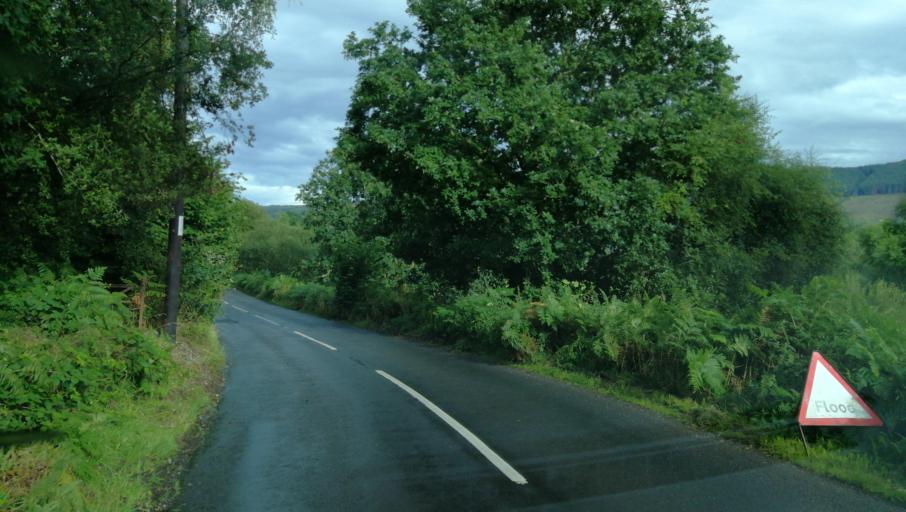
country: GB
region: Scotland
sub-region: Stirling
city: Callander
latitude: 56.2255
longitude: -4.3037
